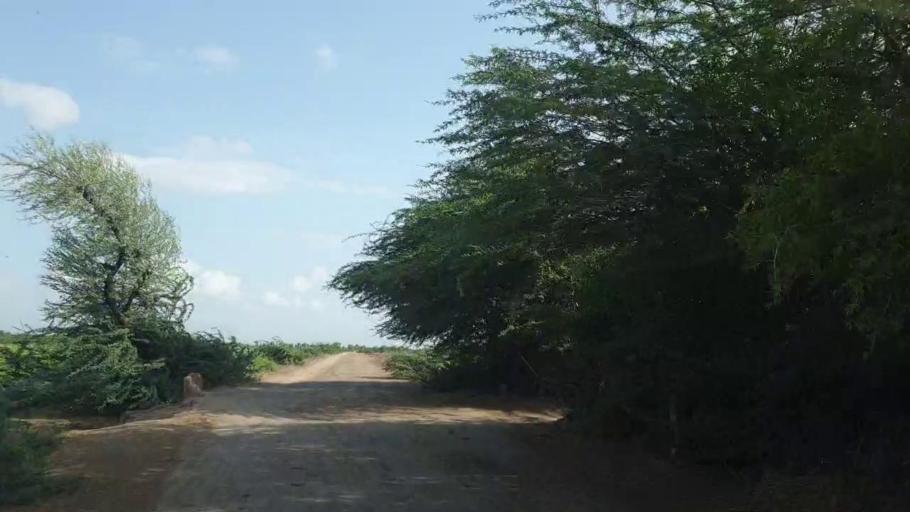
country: PK
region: Sindh
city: Kadhan
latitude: 24.6369
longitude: 69.0960
